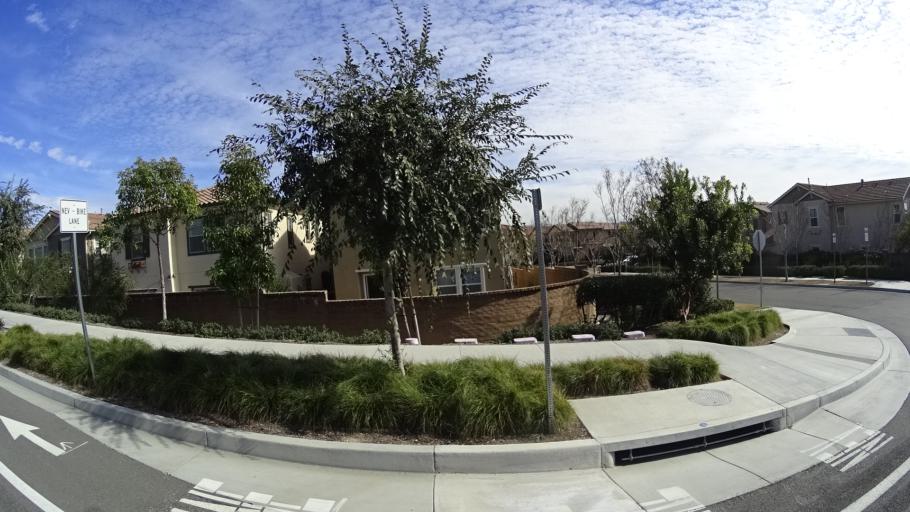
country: US
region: California
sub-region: Orange County
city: Ladera Ranch
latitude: 33.5389
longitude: -117.5964
